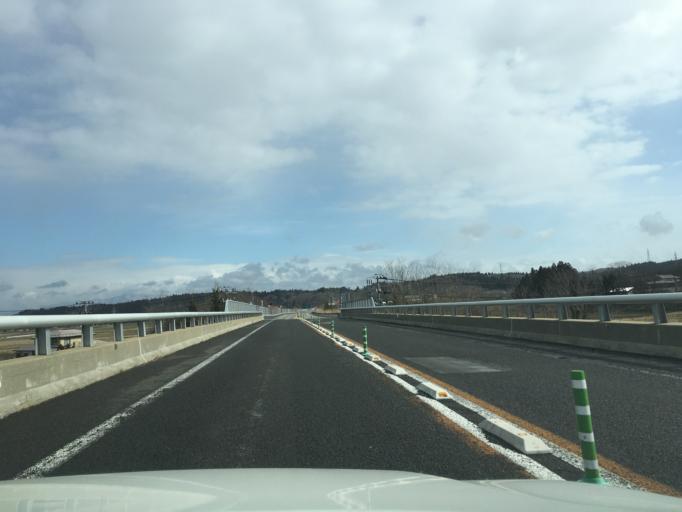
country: JP
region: Akita
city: Akita
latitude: 39.6222
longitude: 140.1525
